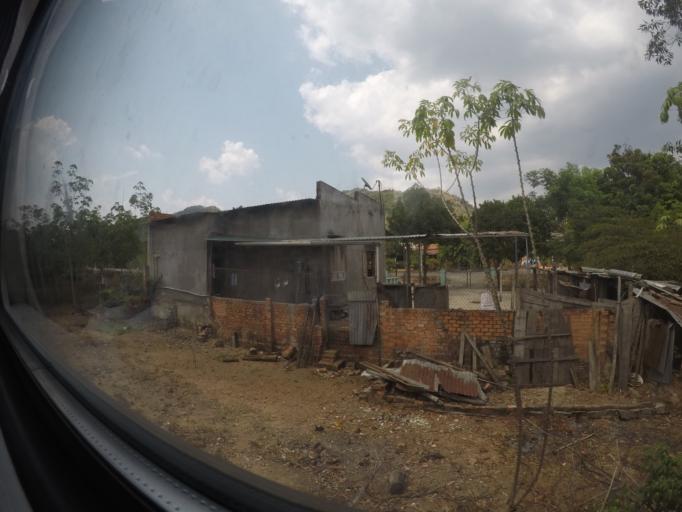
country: VN
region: Binh Thuan
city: Tanh Linh
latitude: 10.9703
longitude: 107.6281
